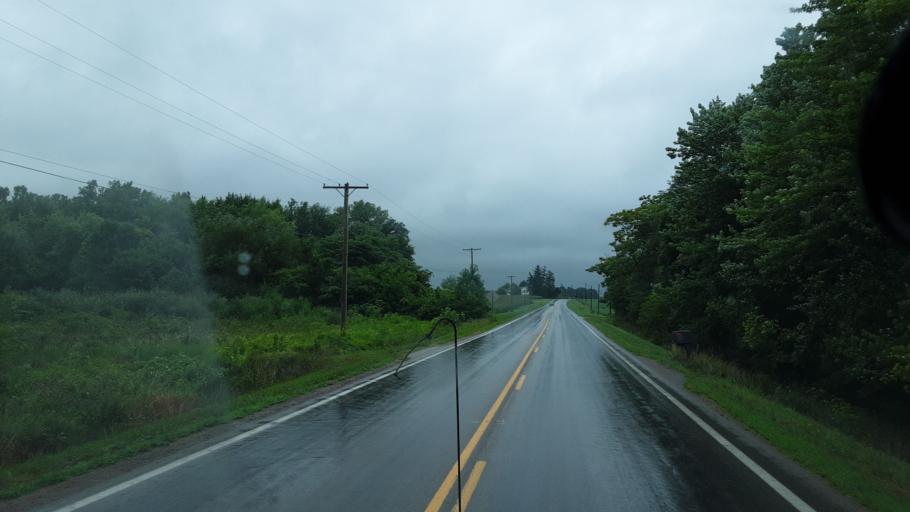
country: US
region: Ohio
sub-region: Mercer County
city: Rockford
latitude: 40.7490
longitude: -84.7878
